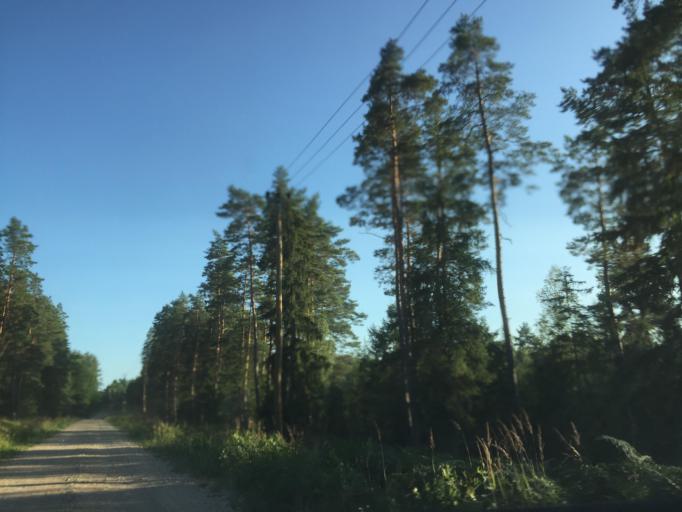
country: LV
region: Talsu Rajons
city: Stende
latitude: 57.1687
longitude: 22.2995
